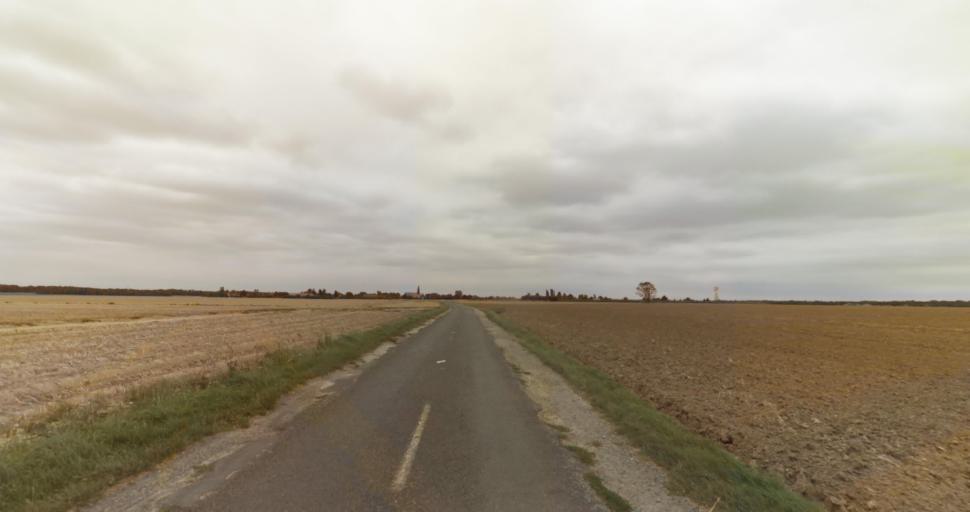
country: FR
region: Haute-Normandie
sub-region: Departement de l'Eure
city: La Couture-Boussey
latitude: 48.9152
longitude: 1.3397
